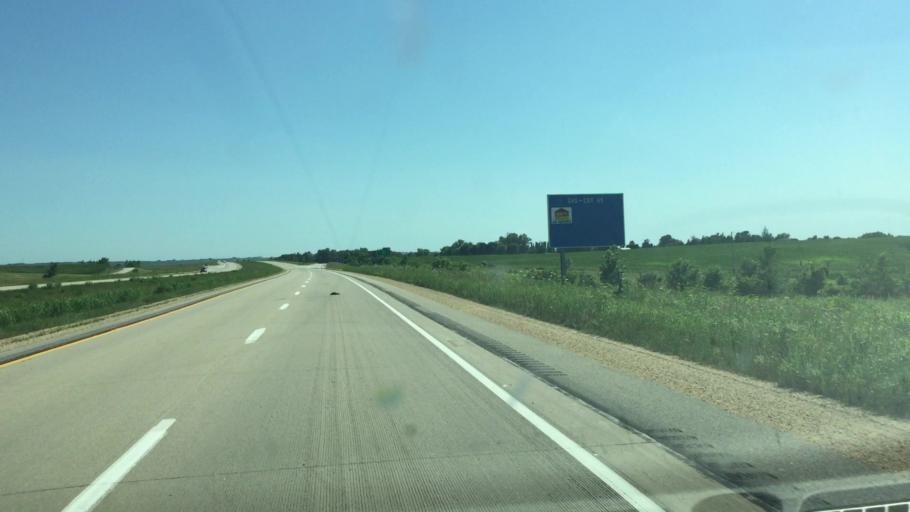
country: US
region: Iowa
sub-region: Jones County
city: Monticello
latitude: 42.2394
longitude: -91.1684
